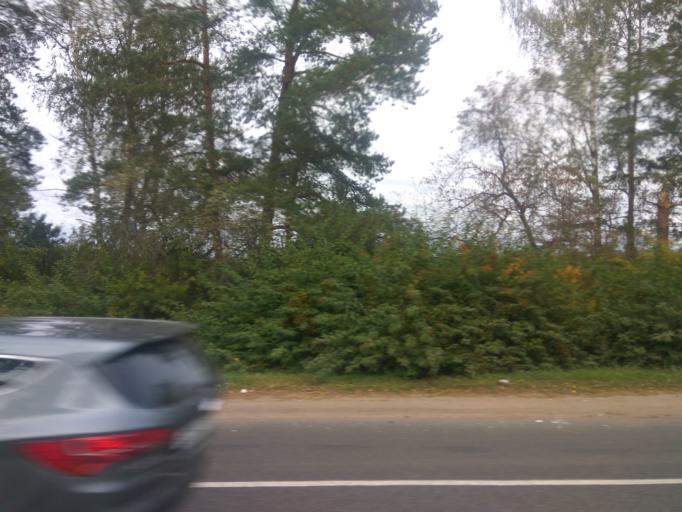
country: RU
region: Moskovskaya
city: Krasnoarmeysk
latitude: 56.0103
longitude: 38.1499
